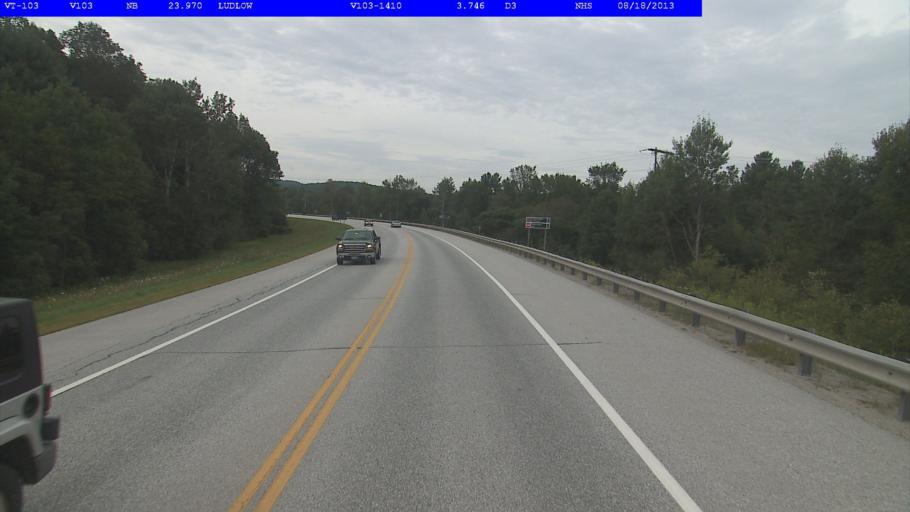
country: US
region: Vermont
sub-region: Windsor County
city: Chester
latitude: 43.4159
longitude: -72.7049
